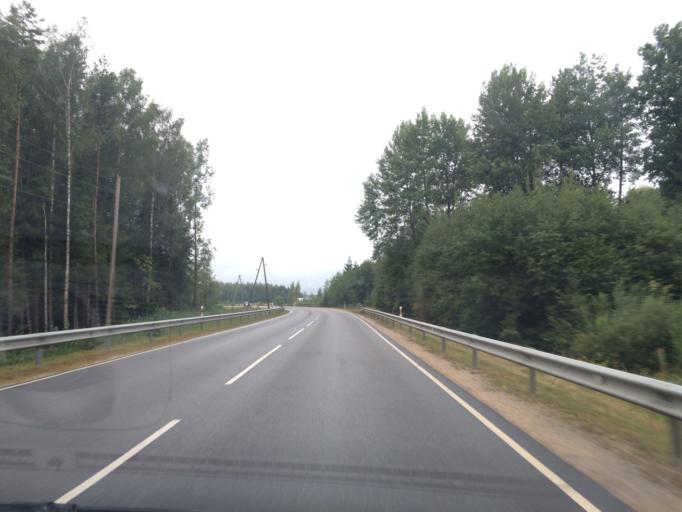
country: LV
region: Ogre
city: Ogre
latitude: 56.8594
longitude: 24.6296
